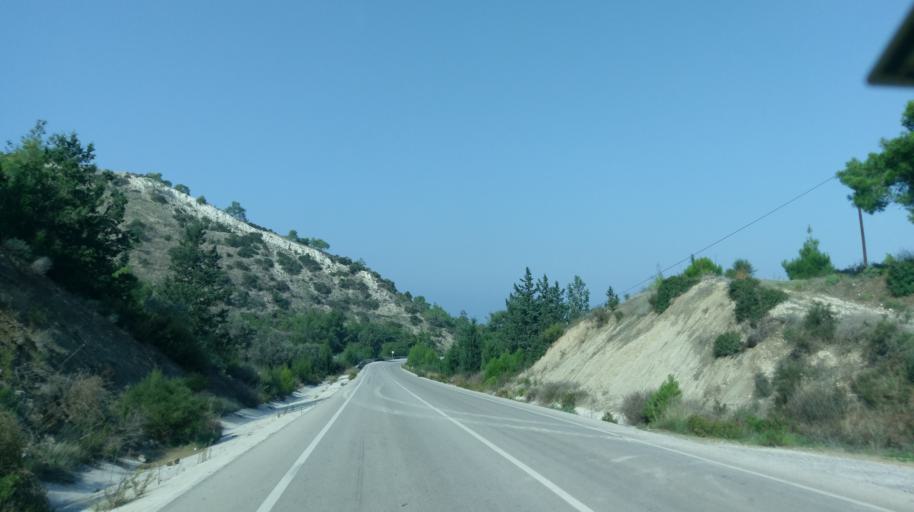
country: CY
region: Ammochostos
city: Lefkonoiko
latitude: 35.3619
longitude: 33.7108
